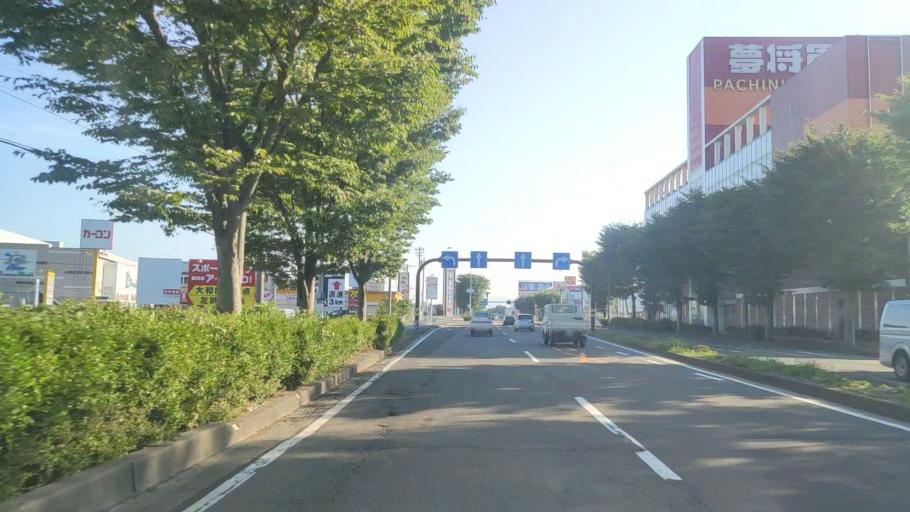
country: JP
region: Fukui
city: Fukui-shi
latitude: 36.0933
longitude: 136.2506
